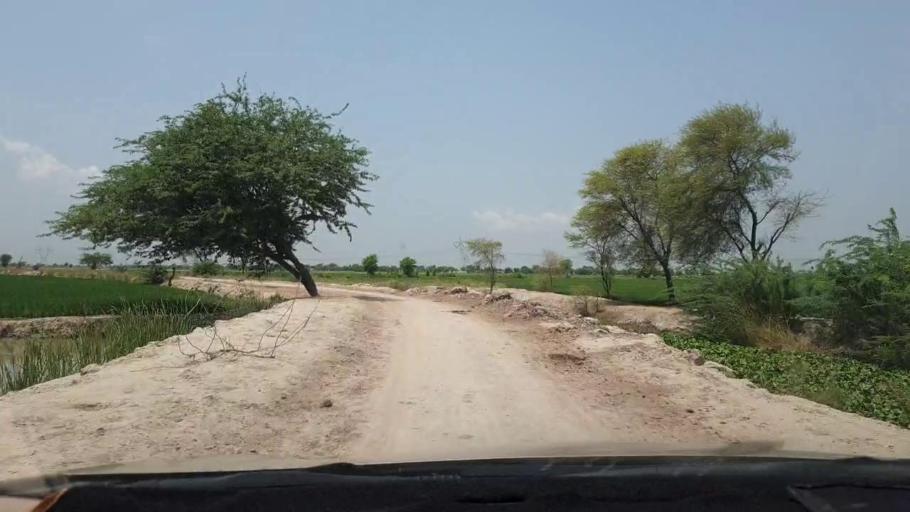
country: PK
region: Sindh
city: Naudero
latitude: 27.6720
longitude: 68.2966
